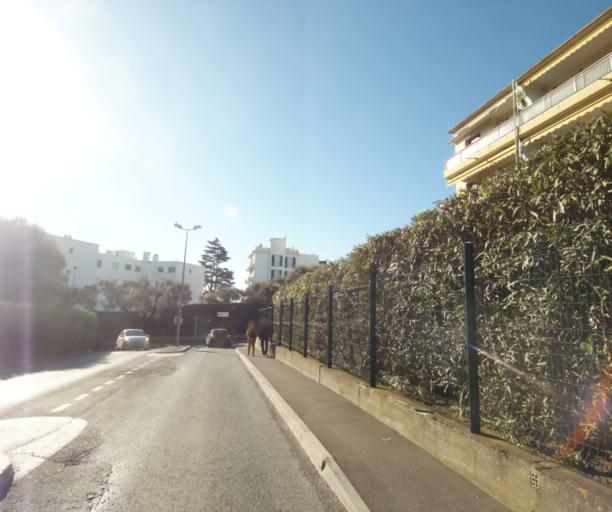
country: FR
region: Provence-Alpes-Cote d'Azur
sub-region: Departement des Alpes-Maritimes
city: Antibes
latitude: 43.5756
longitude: 7.1070
